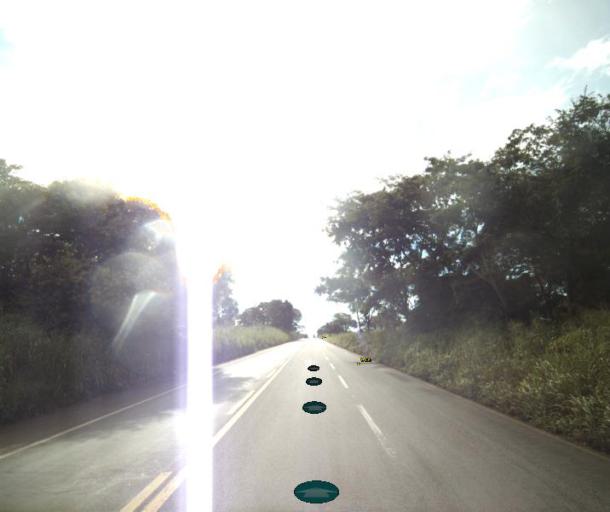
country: BR
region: Goias
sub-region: Jaragua
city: Jaragua
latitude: -15.6299
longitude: -49.3816
